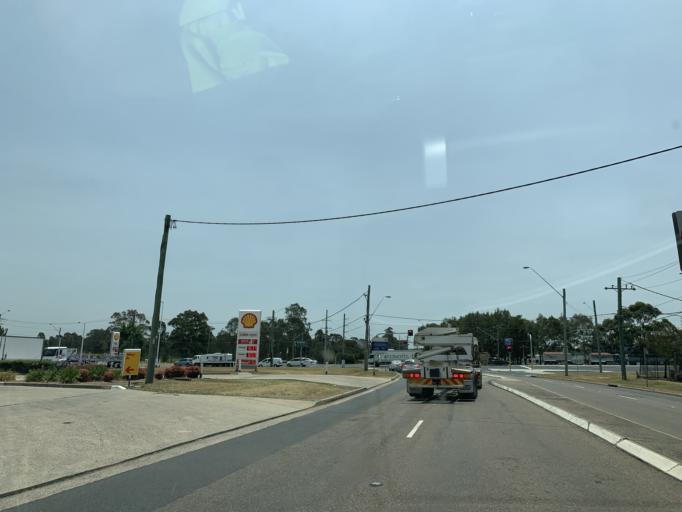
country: AU
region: New South Wales
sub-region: Blacktown
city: Doonside
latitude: -33.7934
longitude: 150.8714
